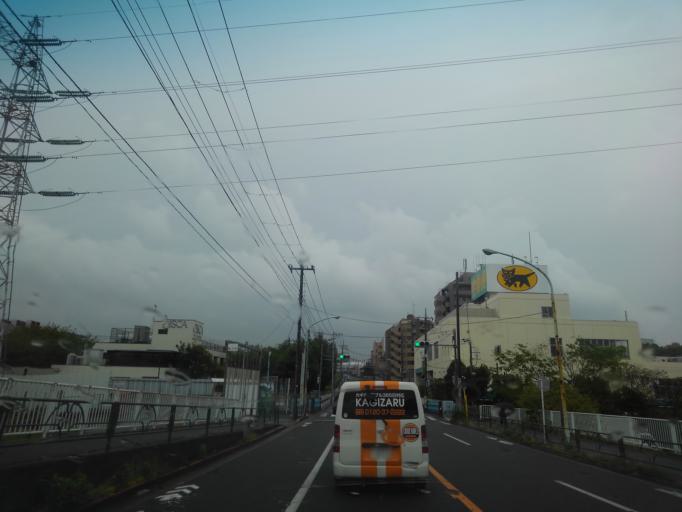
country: JP
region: Tokyo
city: Tokyo
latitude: 35.6743
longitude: 139.6473
